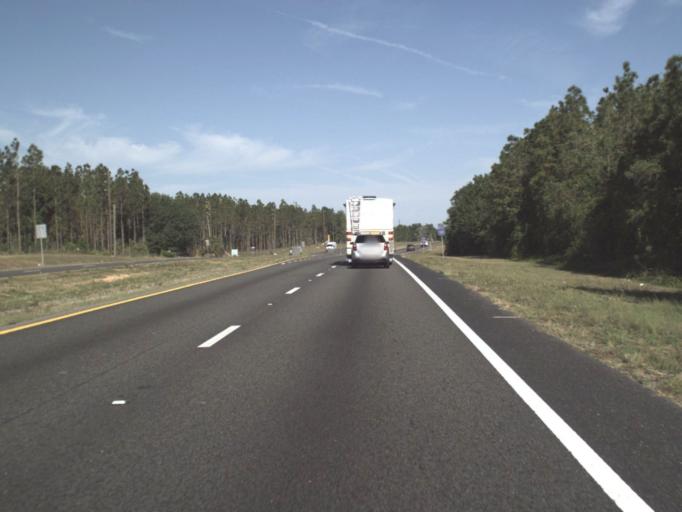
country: US
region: Florida
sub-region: Lake County
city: Mascotte
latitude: 28.6561
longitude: -81.8446
